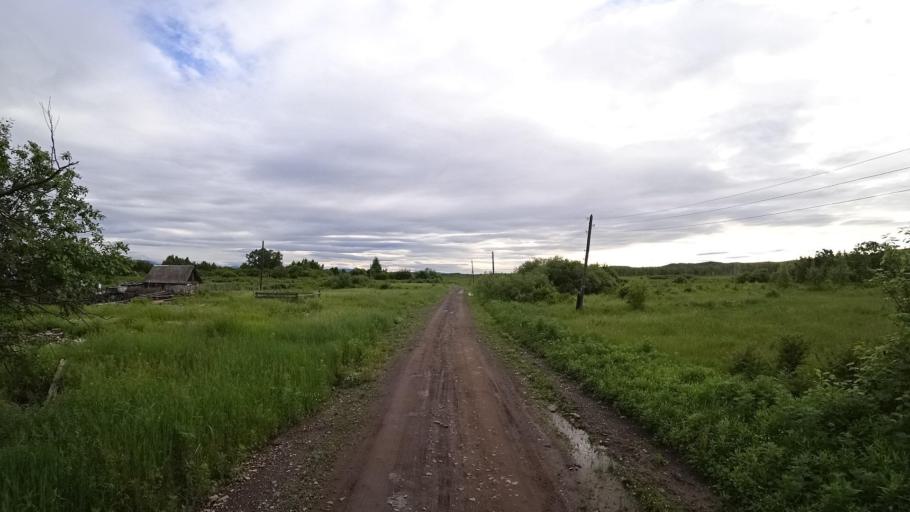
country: RU
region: Khabarovsk Krai
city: Amursk
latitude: 49.8837
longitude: 136.1279
